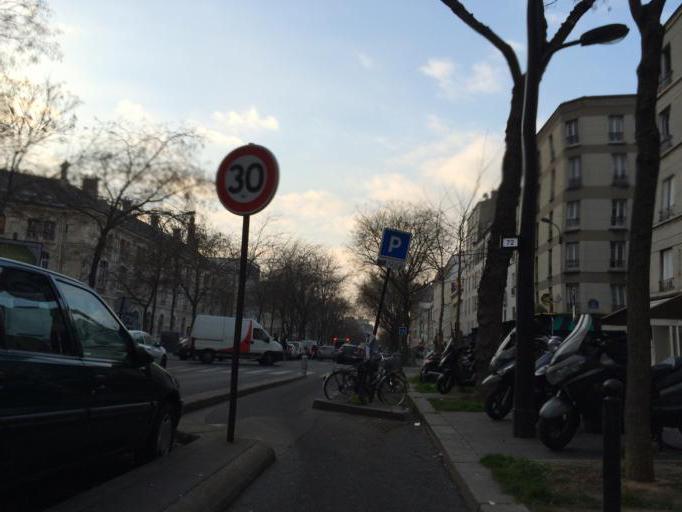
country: FR
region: Ile-de-France
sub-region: Departement de Seine-Saint-Denis
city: Le Pre-Saint-Gervais
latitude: 48.8638
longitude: 2.3865
